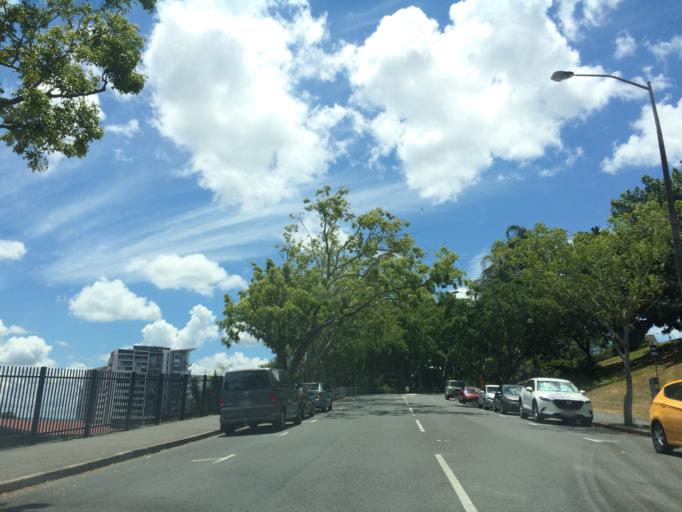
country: AU
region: Queensland
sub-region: Brisbane
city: Spring Hill
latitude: -27.4657
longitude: 153.0213
